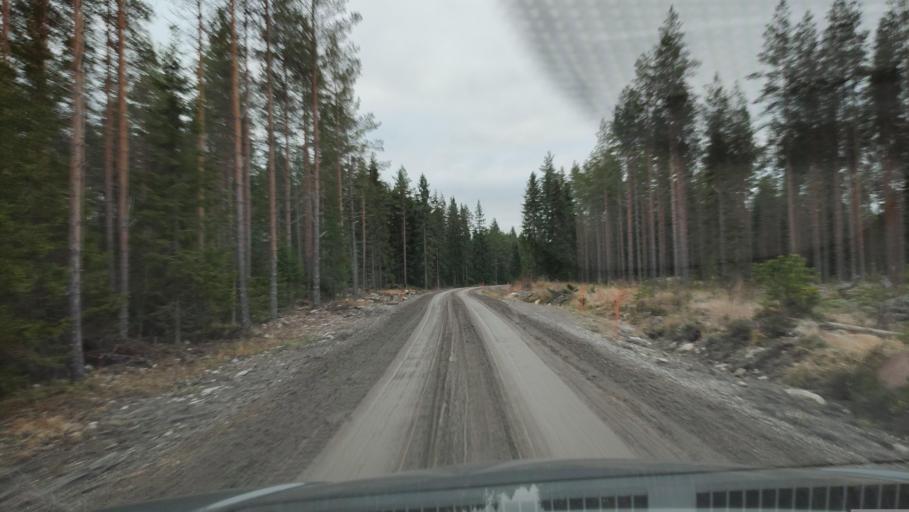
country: FI
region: Southern Ostrobothnia
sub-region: Suupohja
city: Karijoki
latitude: 62.1911
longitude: 21.5886
